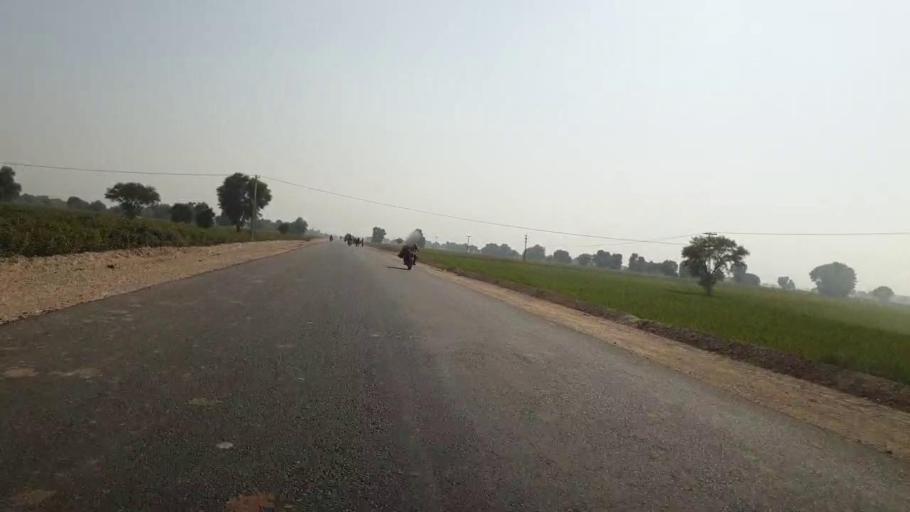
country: PK
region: Sindh
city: Dadu
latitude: 26.6734
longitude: 67.7765
